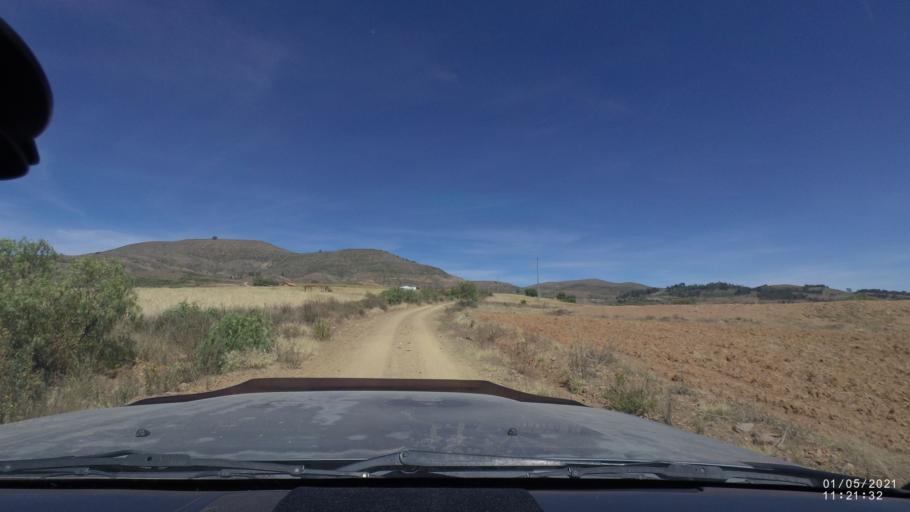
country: BO
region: Cochabamba
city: Tarata
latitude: -17.6457
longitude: -66.1273
